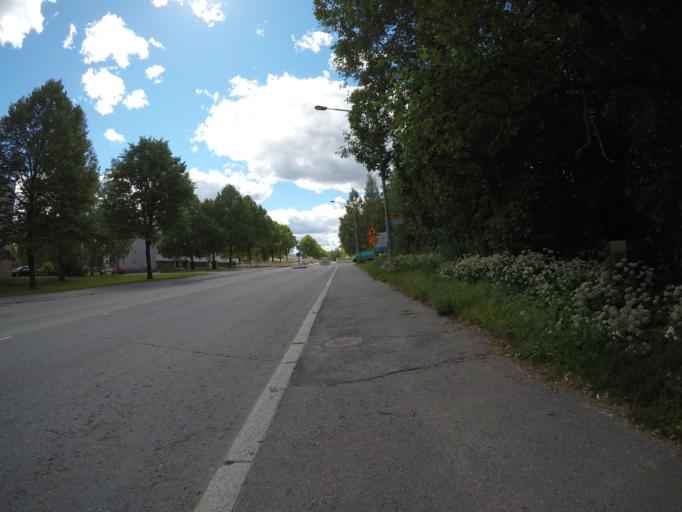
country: FI
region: Haeme
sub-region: Haemeenlinna
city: Haemeenlinna
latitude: 61.0084
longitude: 24.4447
